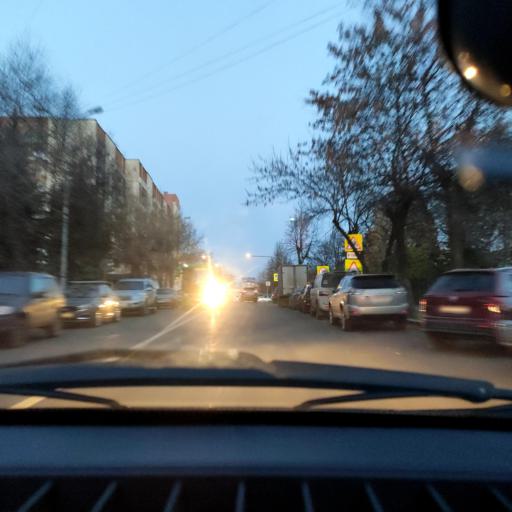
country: RU
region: Bashkortostan
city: Ufa
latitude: 54.7301
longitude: 55.9722
